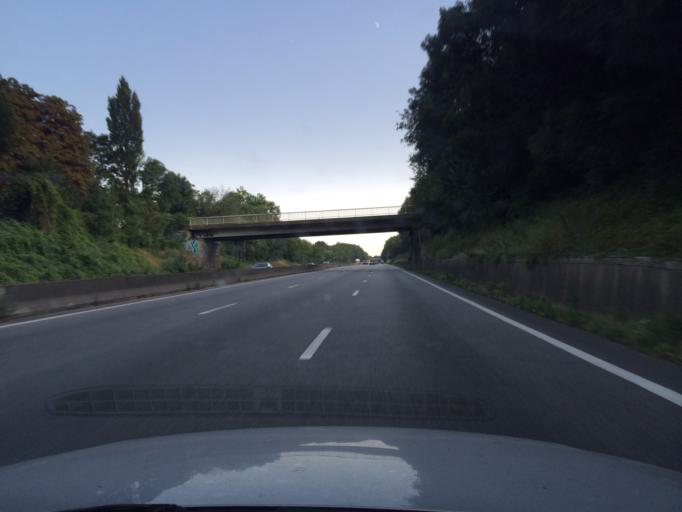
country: FR
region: Ile-de-France
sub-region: Departement des Yvelines
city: Orgeval
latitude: 48.9114
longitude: 2.0054
